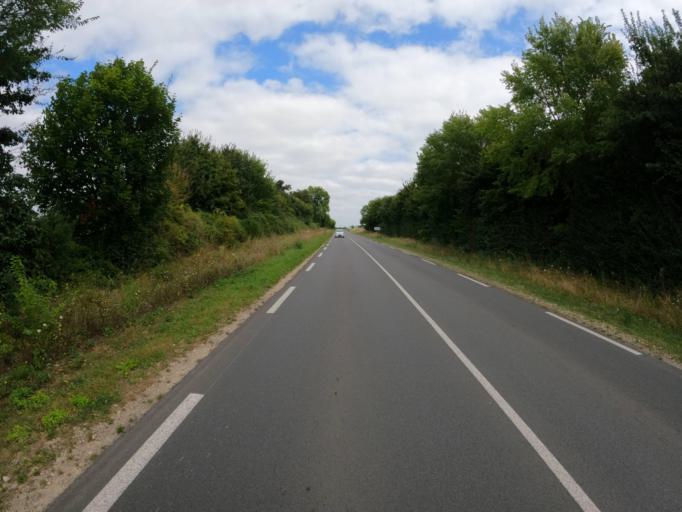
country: FR
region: Poitou-Charentes
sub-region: Departement de la Vienne
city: Civray
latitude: 46.1601
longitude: 0.2943
